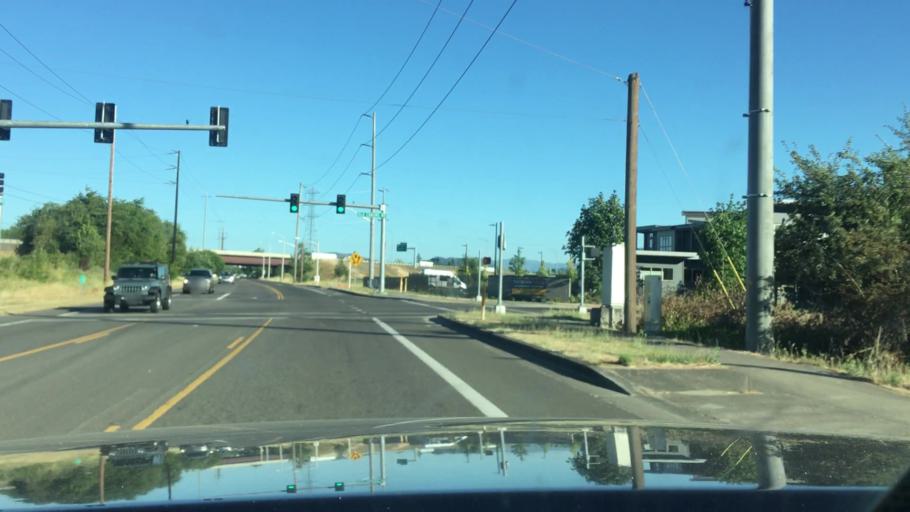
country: US
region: Oregon
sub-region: Lane County
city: Coburg
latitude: 44.0912
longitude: -123.0491
